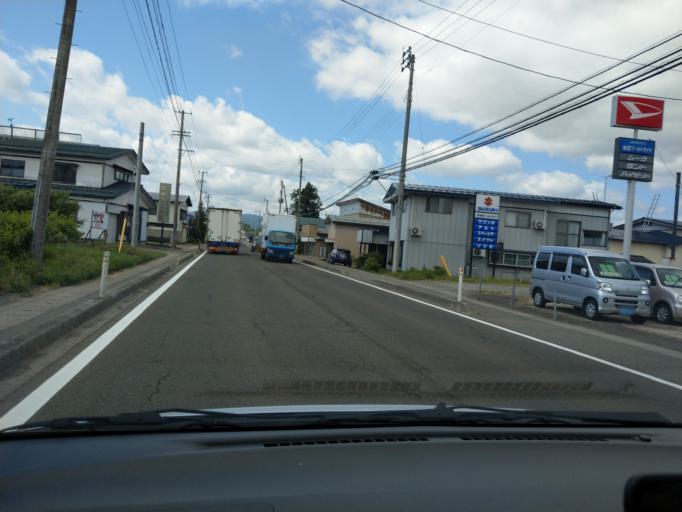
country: JP
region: Akita
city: Yuzawa
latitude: 39.1869
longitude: 140.5003
